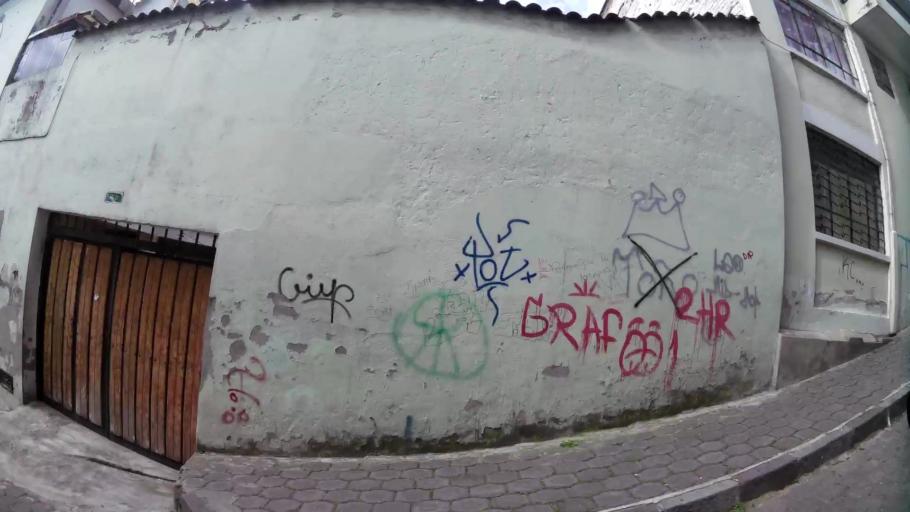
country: EC
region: Pichincha
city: Quito
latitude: -0.2178
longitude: -78.5036
